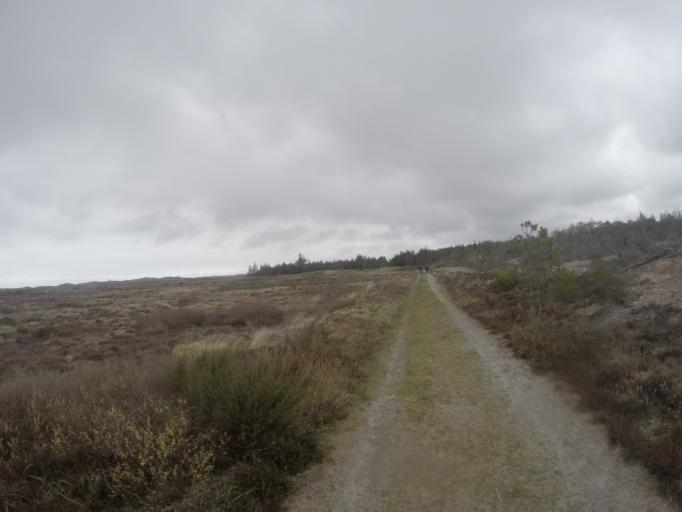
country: DK
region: North Denmark
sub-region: Thisted Kommune
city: Hurup
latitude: 56.9085
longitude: 8.3475
